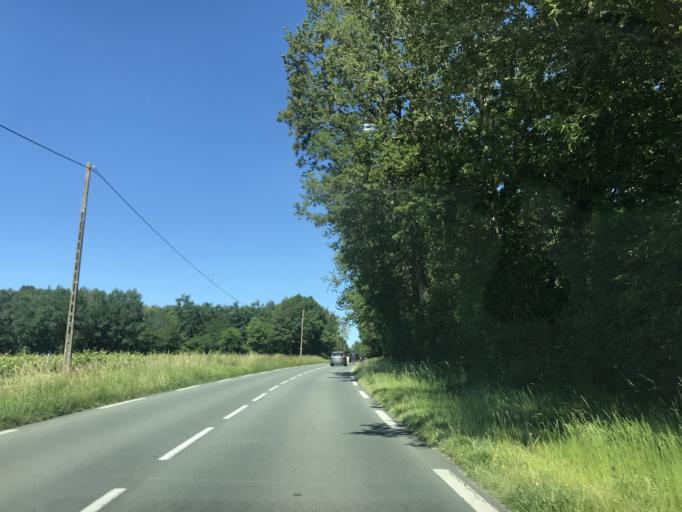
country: FR
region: Poitou-Charentes
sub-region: Departement de la Charente-Maritime
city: Cozes
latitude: 45.5778
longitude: -0.7819
